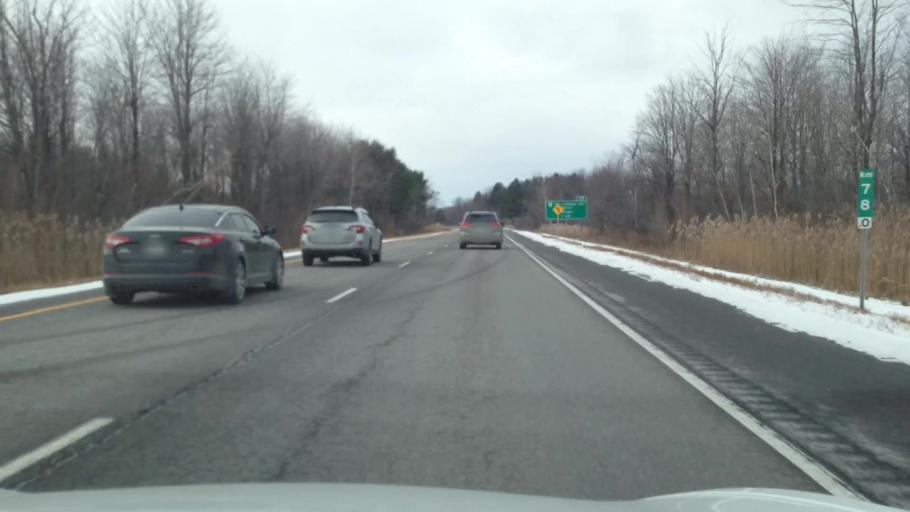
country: CA
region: Ontario
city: Bourget
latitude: 45.3133
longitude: -75.2240
